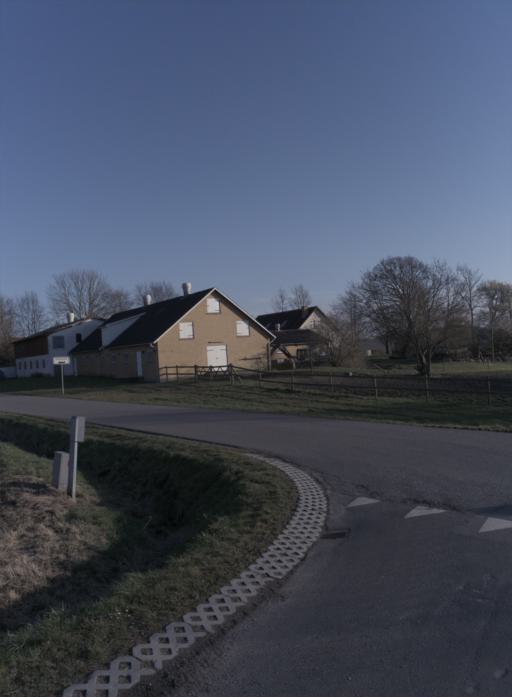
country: DK
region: Zealand
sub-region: Kalundborg Kommune
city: Kalundborg
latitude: 55.6910
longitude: 11.1568
